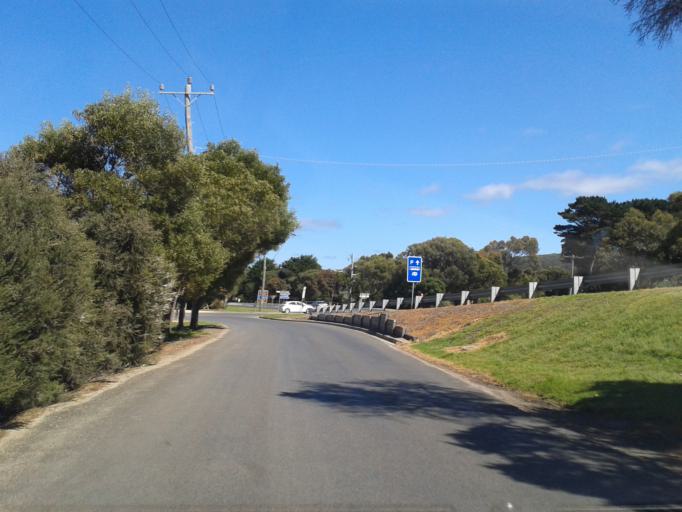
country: AU
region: Victoria
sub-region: Surf Coast
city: Anglesea
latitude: -38.4643
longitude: 144.1024
